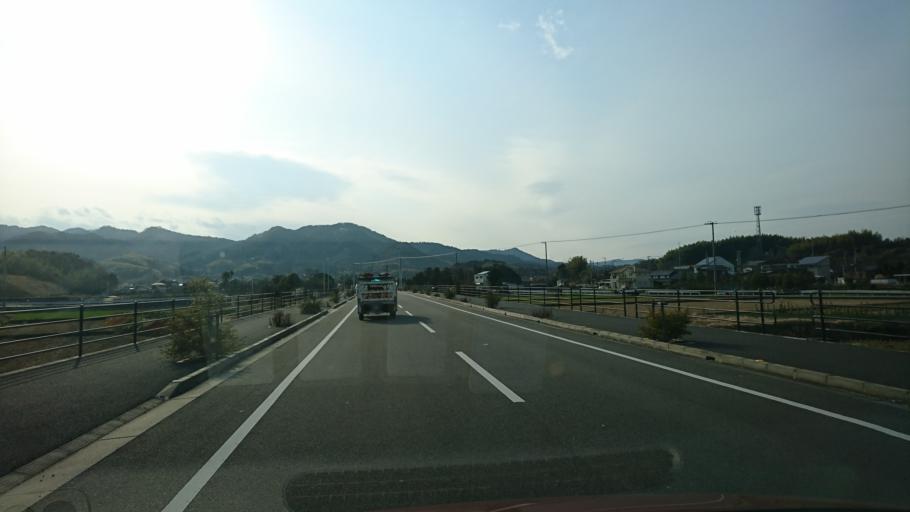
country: JP
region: Ehime
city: Saijo
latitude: 34.0235
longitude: 132.9976
